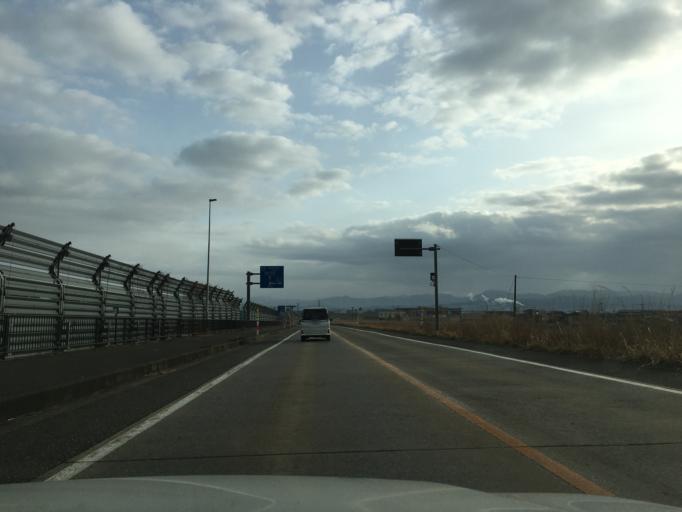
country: JP
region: Yamagata
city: Sakata
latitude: 38.8268
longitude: 139.8418
